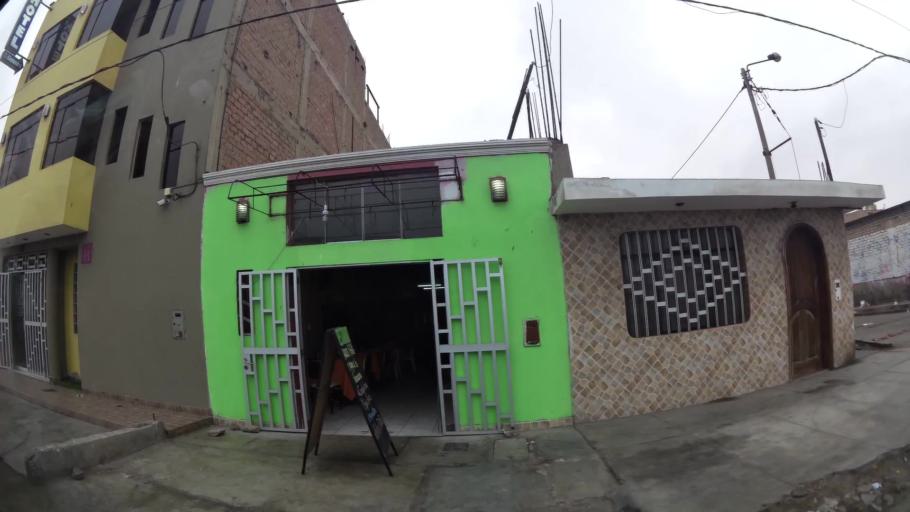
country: PE
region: Ica
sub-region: Provincia de Pisco
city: Pisco
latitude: -13.7342
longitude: -76.2246
